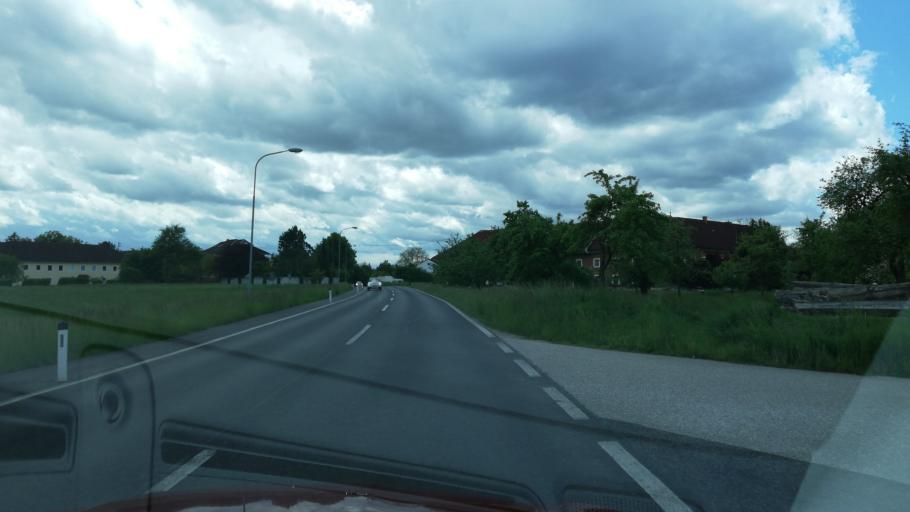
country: AT
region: Upper Austria
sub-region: Politischer Bezirk Linz-Land
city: Ansfelden
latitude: 48.1996
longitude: 14.2621
